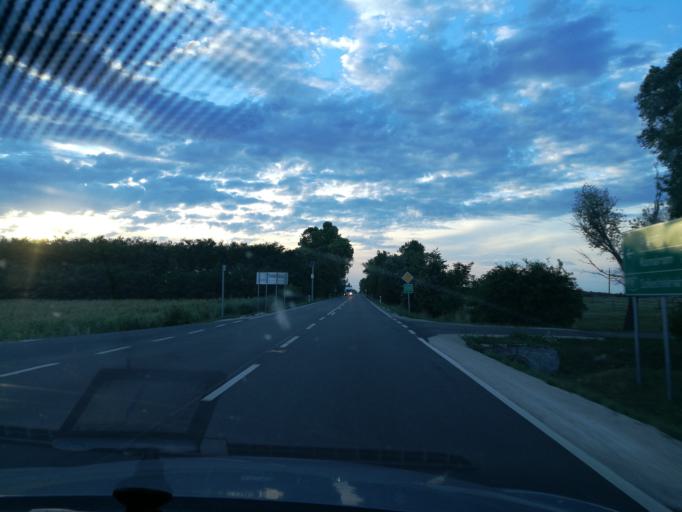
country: HU
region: Komarom-Esztergom
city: Csaszar
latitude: 47.4486
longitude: 18.1053
